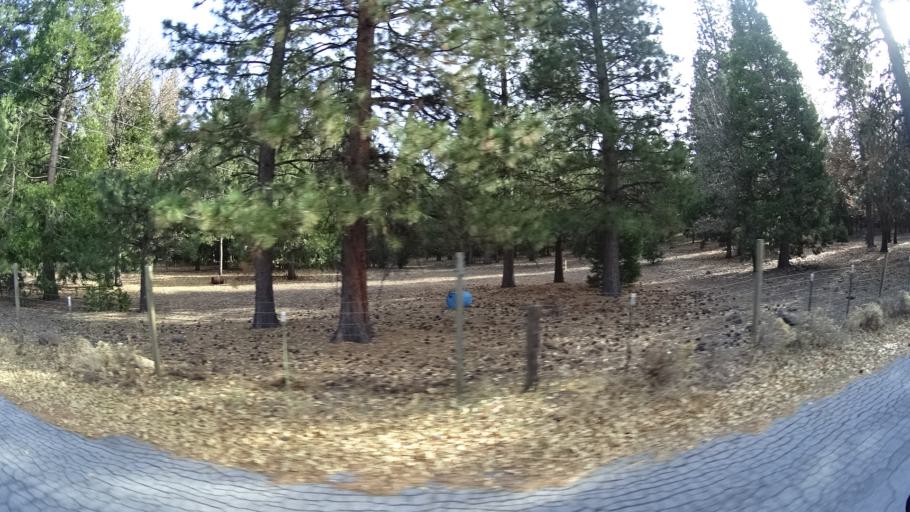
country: US
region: California
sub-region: Siskiyou County
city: Weed
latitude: 41.4467
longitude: -122.3801
